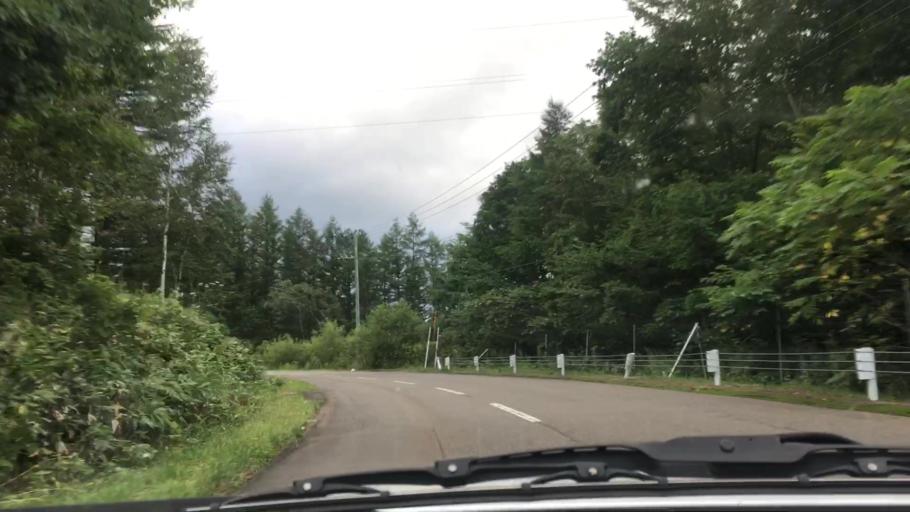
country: JP
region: Hokkaido
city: Otofuke
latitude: 43.1571
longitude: 142.8542
